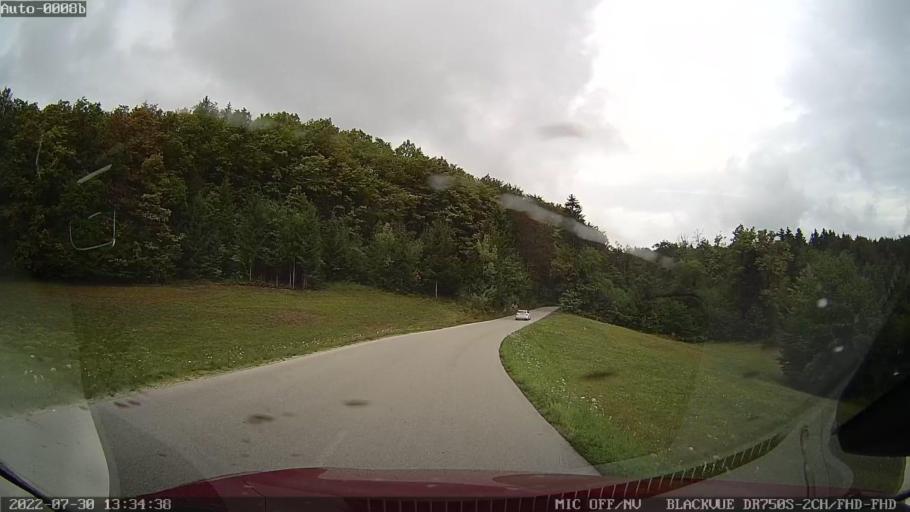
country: SI
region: Zuzemberk
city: Zuzemberk
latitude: 45.8589
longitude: 14.9286
